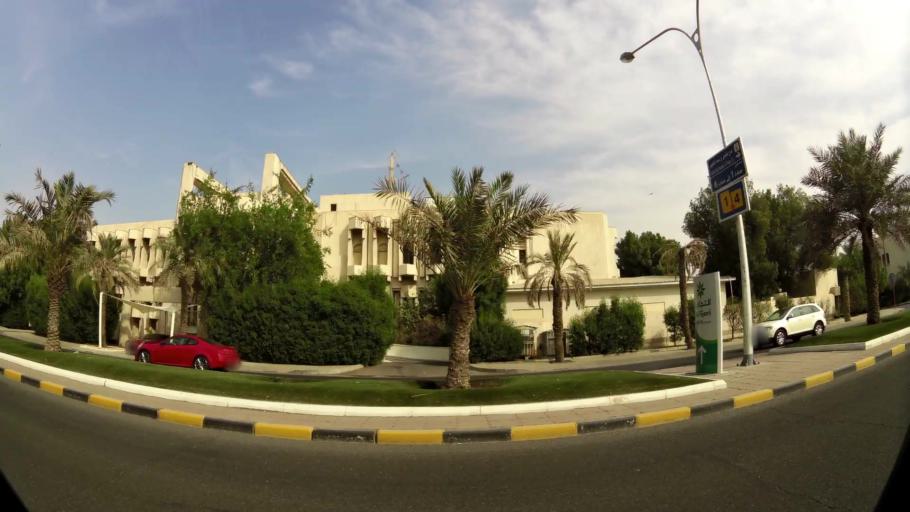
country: KW
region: Al Asimah
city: Ash Shamiyah
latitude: 29.3167
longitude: 47.9681
